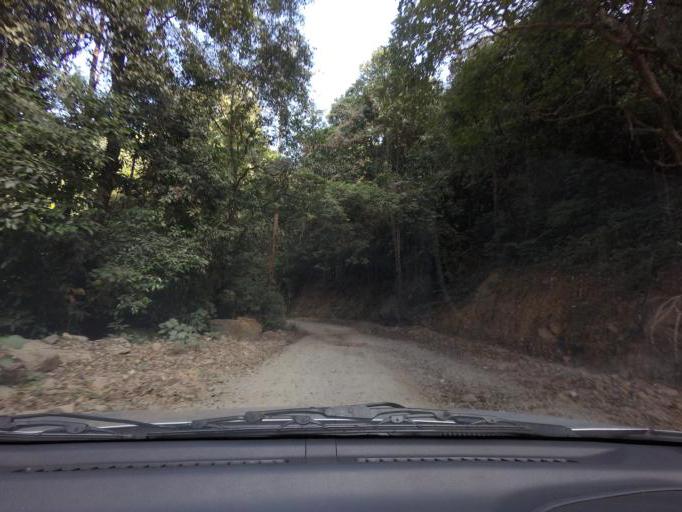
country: IN
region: Karnataka
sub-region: Kodagu
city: Somvarpet
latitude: 12.7123
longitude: 75.6822
